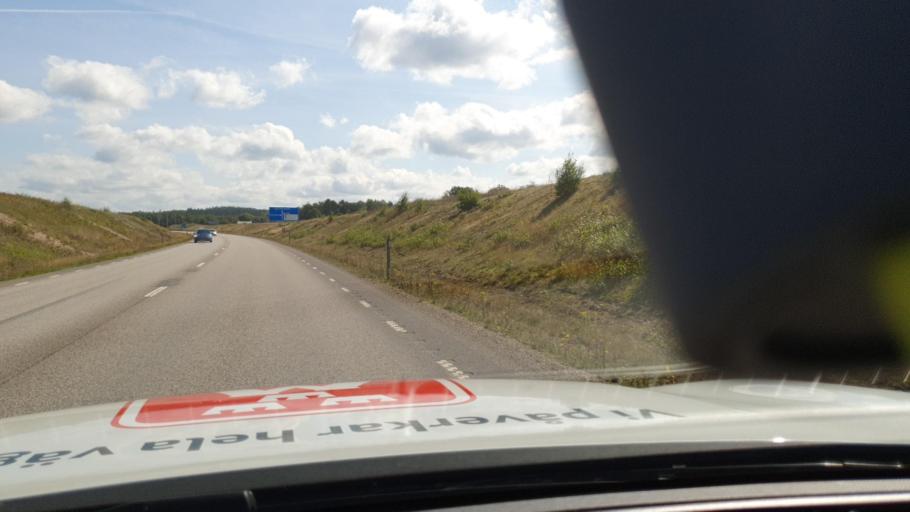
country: SE
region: Halland
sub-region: Laholms Kommun
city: Veinge
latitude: 56.5271
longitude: 13.1774
